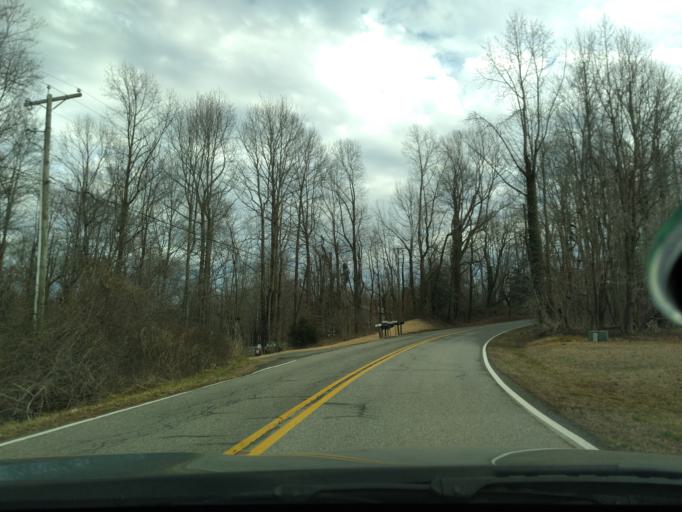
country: US
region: Maryland
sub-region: Calvert County
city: Chesapeake Beach
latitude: 38.6343
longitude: -76.5325
